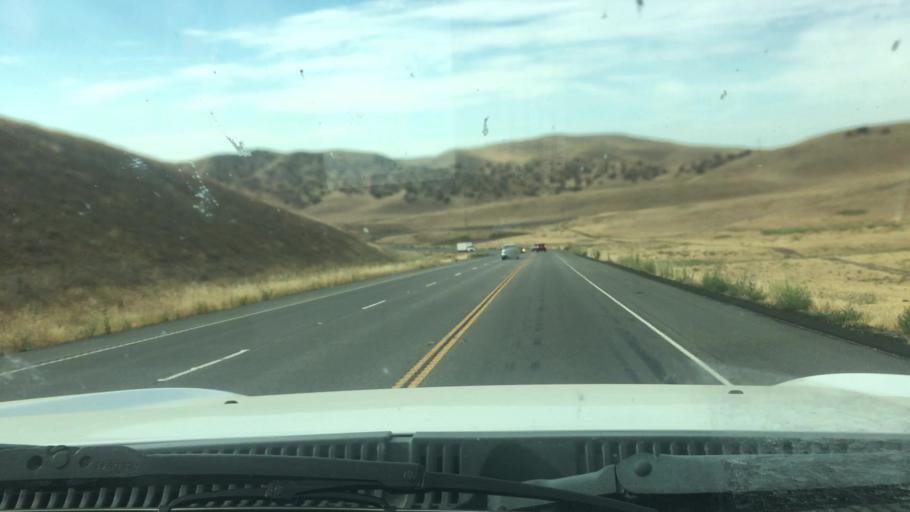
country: US
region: California
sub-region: San Luis Obispo County
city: Shandon
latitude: 35.7370
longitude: -120.2104
